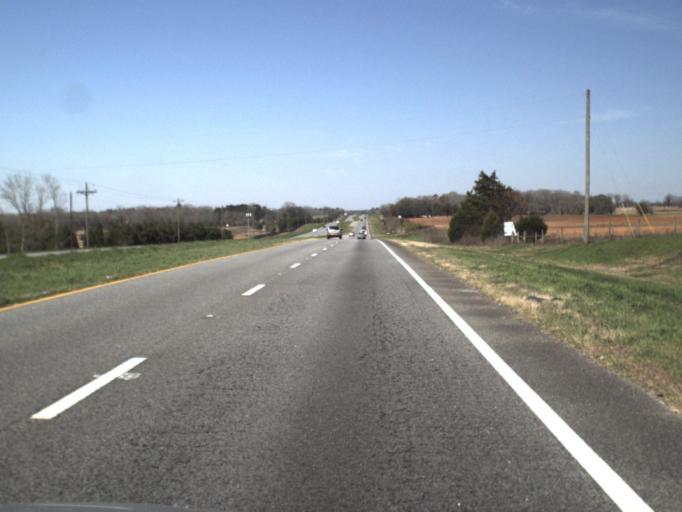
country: US
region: Florida
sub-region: Jackson County
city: Graceville
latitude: 30.9098
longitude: -85.3777
